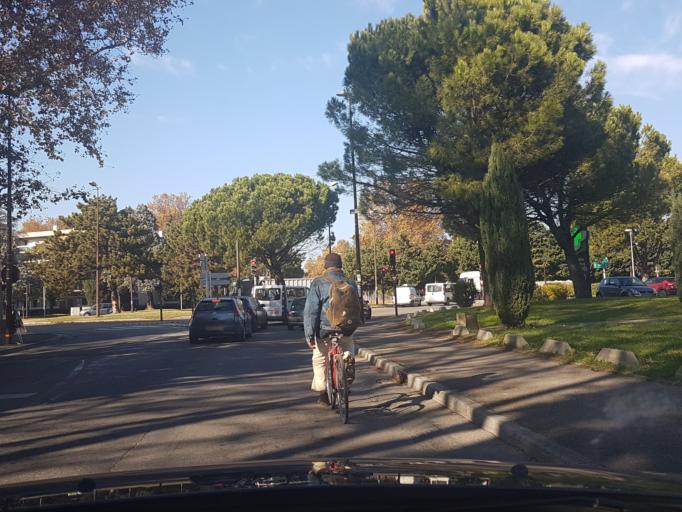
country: FR
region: Provence-Alpes-Cote d'Azur
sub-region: Departement du Vaucluse
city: Avignon
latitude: 43.9315
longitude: 4.8298
